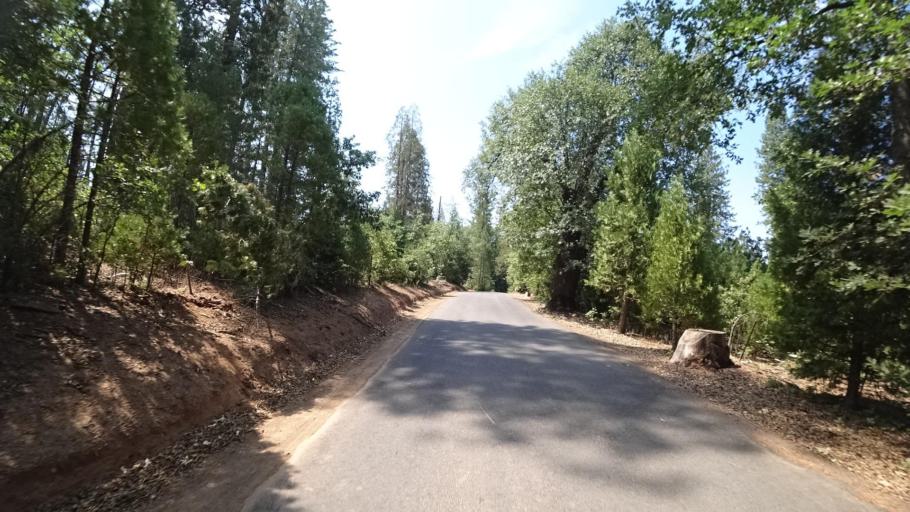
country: US
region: California
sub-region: Mariposa County
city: Midpines
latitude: 37.7176
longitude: -120.0938
